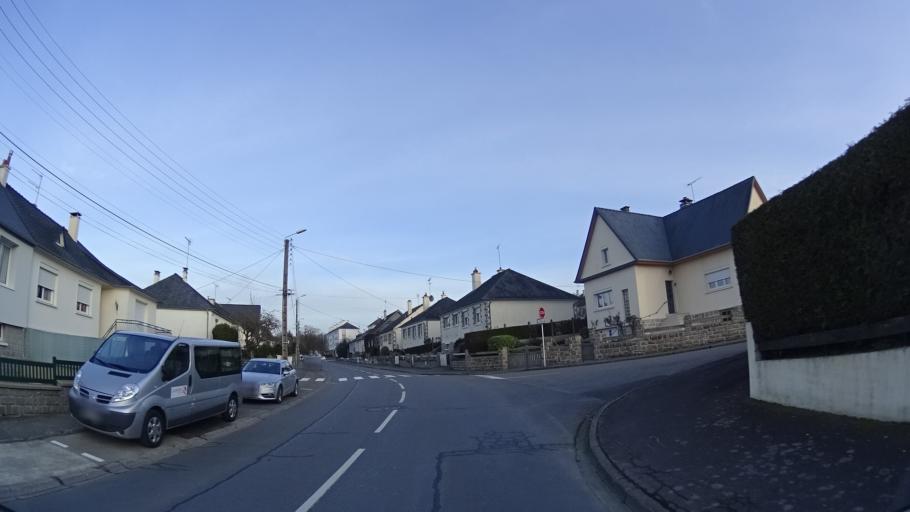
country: FR
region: Brittany
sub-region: Departement d'Ille-et-Vilaine
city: Vitre
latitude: 48.1174
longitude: -1.2146
